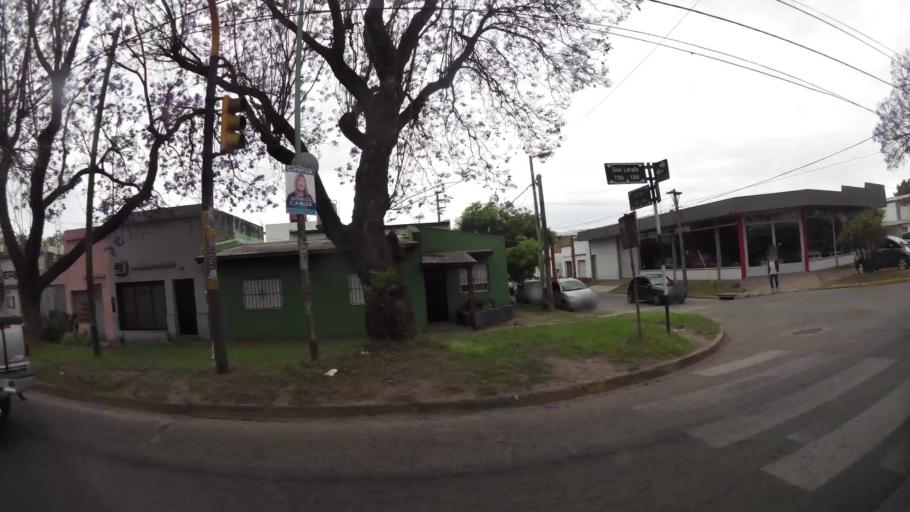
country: AR
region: Buenos Aires
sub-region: Partido de Zarate
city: Zarate
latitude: -34.1065
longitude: -59.0220
